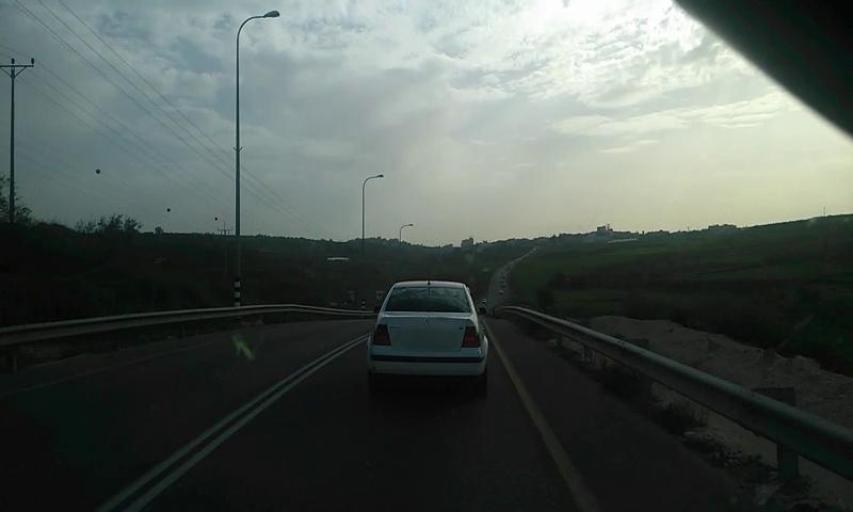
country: PS
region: West Bank
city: Immatin
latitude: 32.1977
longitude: 35.1461
